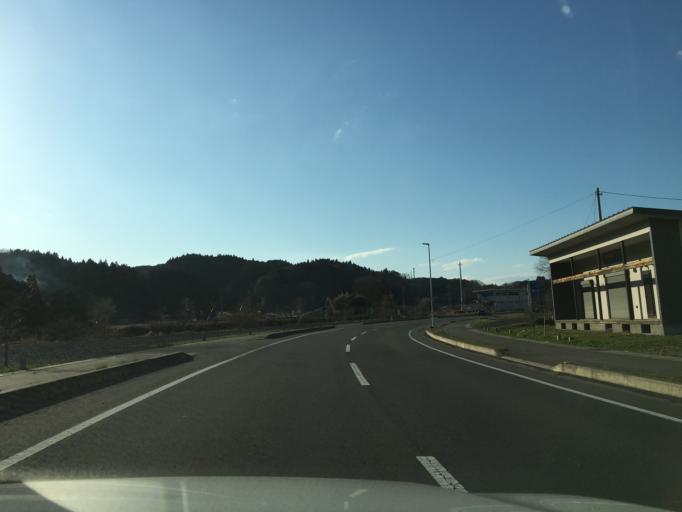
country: JP
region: Ibaraki
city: Daigo
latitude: 36.7687
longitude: 140.3534
